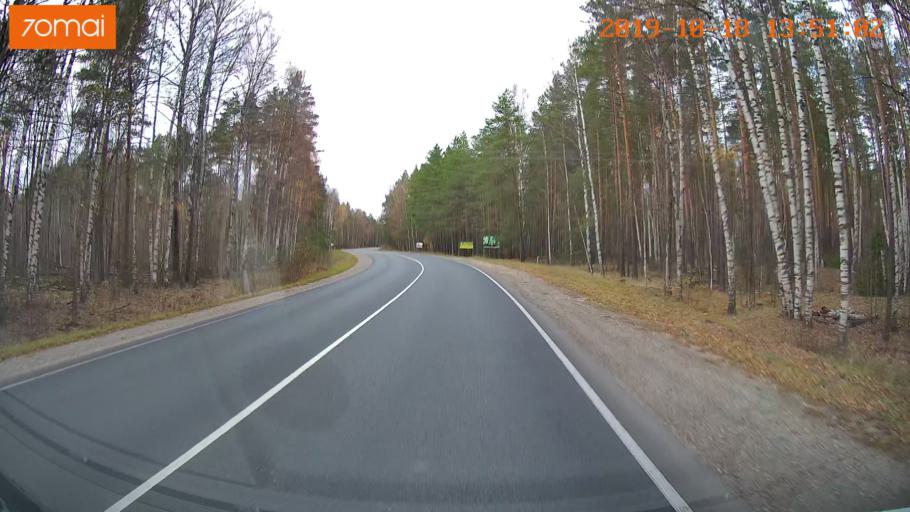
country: RU
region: Moskovskaya
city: Radovitskiy
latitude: 55.0128
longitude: 39.9642
